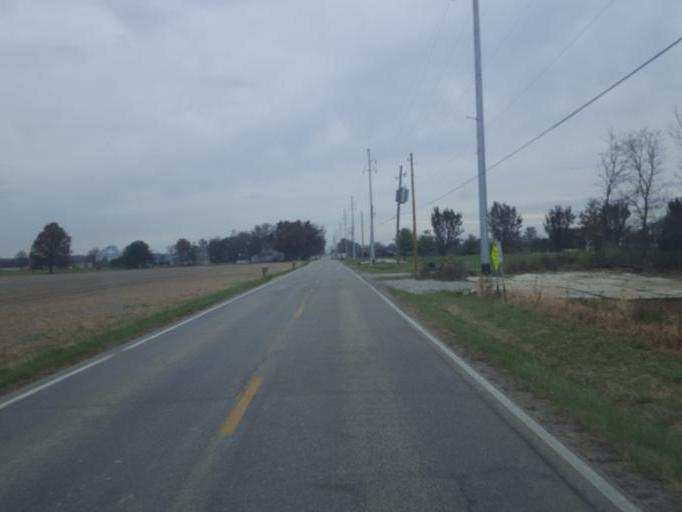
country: US
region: Ohio
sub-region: Delaware County
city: Delaware
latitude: 40.3373
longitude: -83.0996
